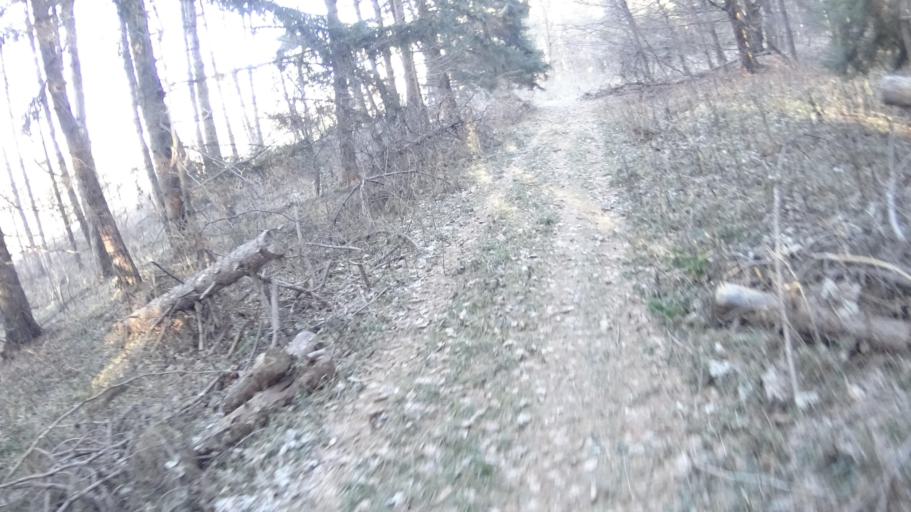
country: HU
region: Heves
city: Szilvasvarad
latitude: 48.0922
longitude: 20.4791
